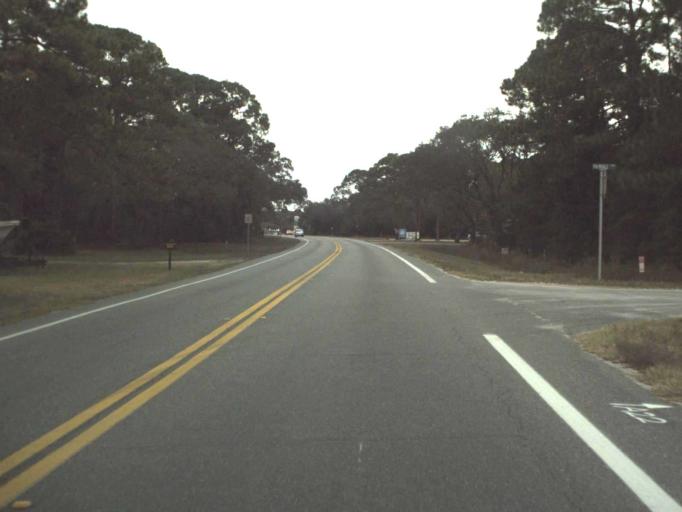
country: US
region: Florida
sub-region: Wakulla County
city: Crawfordville
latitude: 30.0230
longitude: -84.3904
